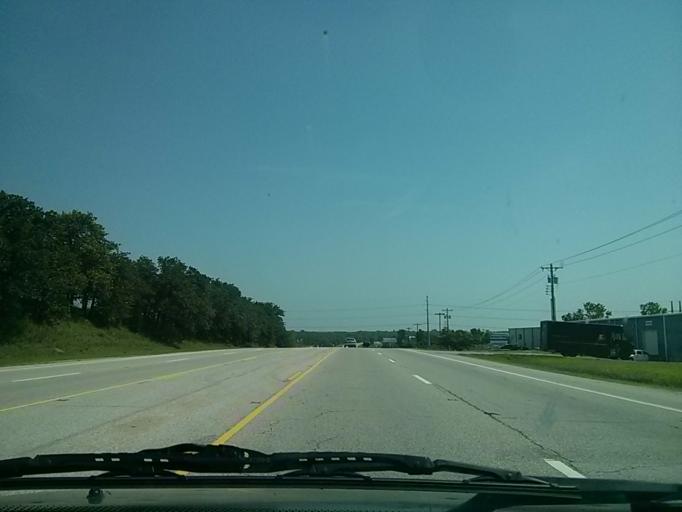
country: US
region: Oklahoma
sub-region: Tulsa County
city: Oakhurst
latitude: 36.0567
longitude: -96.0724
